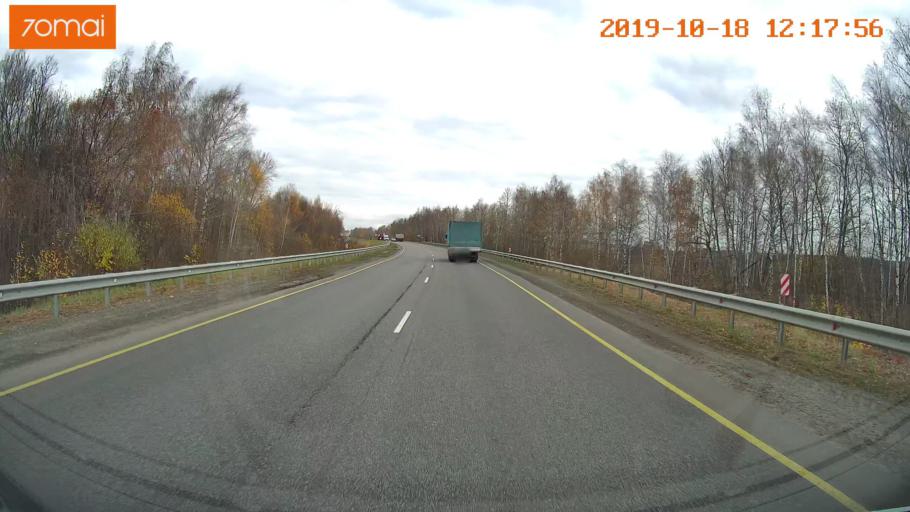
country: RU
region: Rjazan
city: Zakharovo
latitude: 54.4616
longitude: 39.4517
